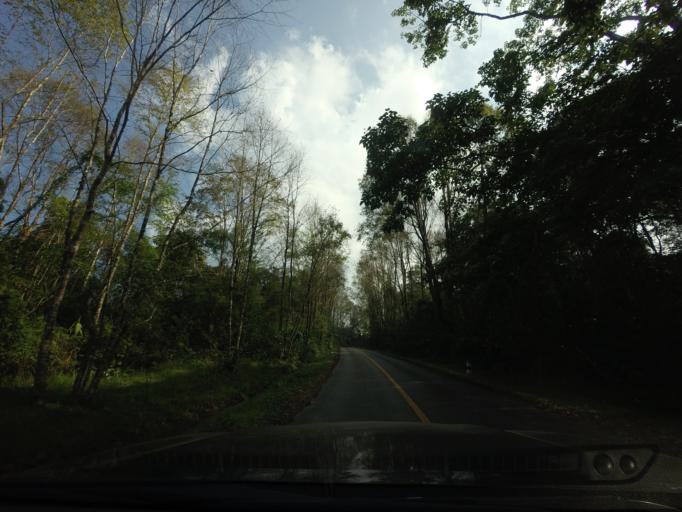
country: TH
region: Phitsanulok
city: Nakhon Thai
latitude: 16.9737
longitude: 101.0190
